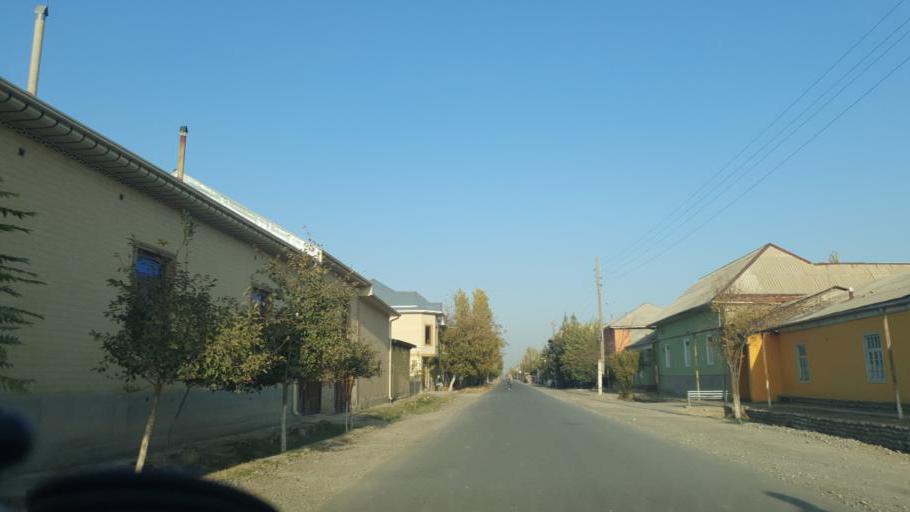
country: UZ
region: Fergana
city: Beshariq
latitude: 40.4635
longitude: 70.5485
